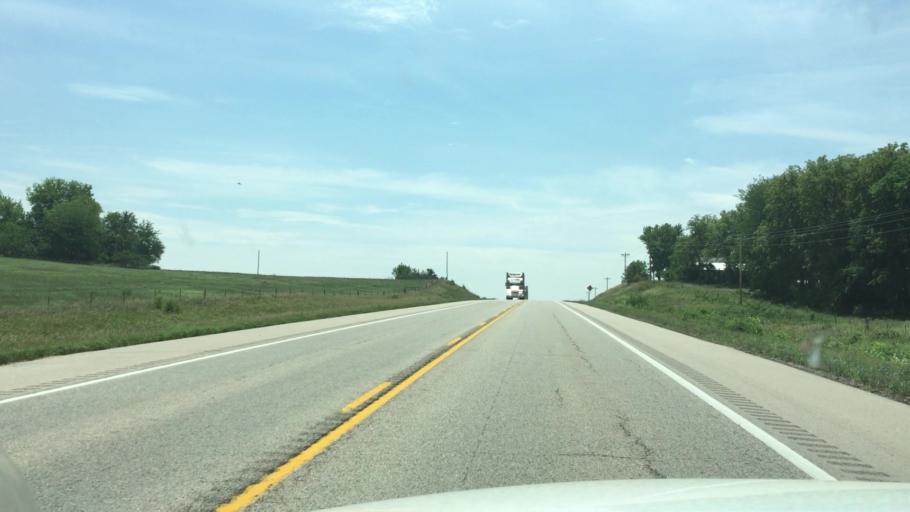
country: US
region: Kansas
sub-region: Jackson County
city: Holton
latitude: 39.6263
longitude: -95.7311
